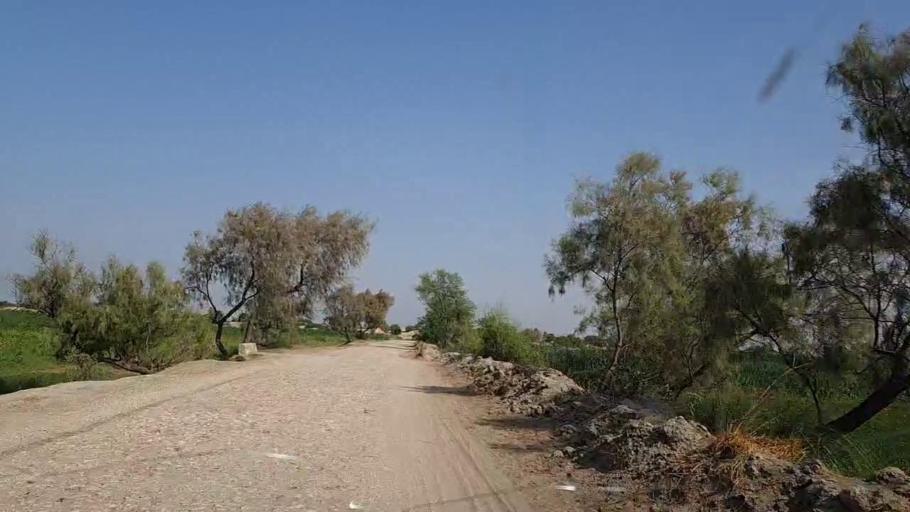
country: PK
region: Sindh
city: Khanpur
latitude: 27.7326
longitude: 69.3569
